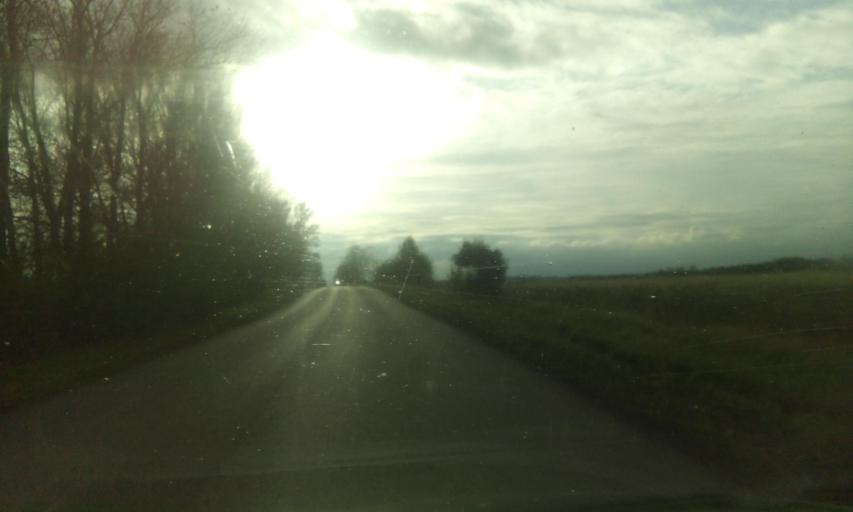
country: RU
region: Tula
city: Partizan
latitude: 53.9704
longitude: 38.1090
